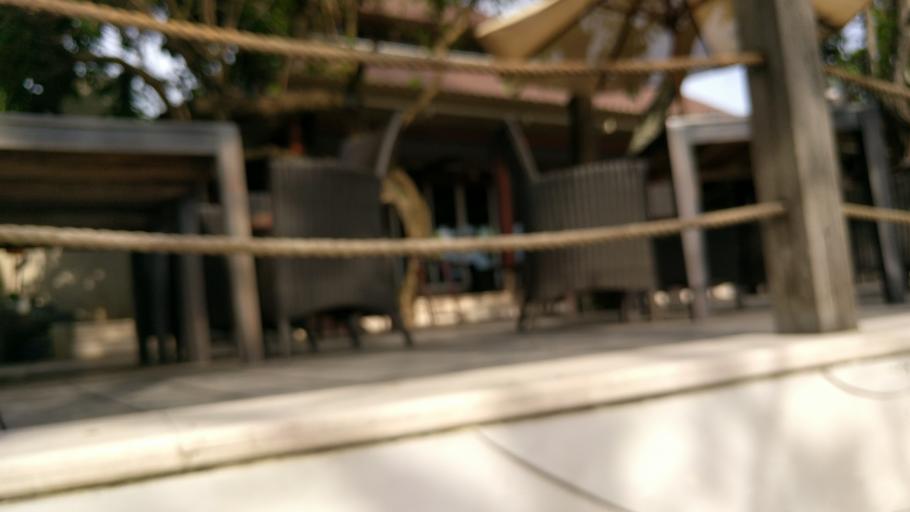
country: ID
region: Bali
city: Kuta
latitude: -8.6930
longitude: 115.1588
